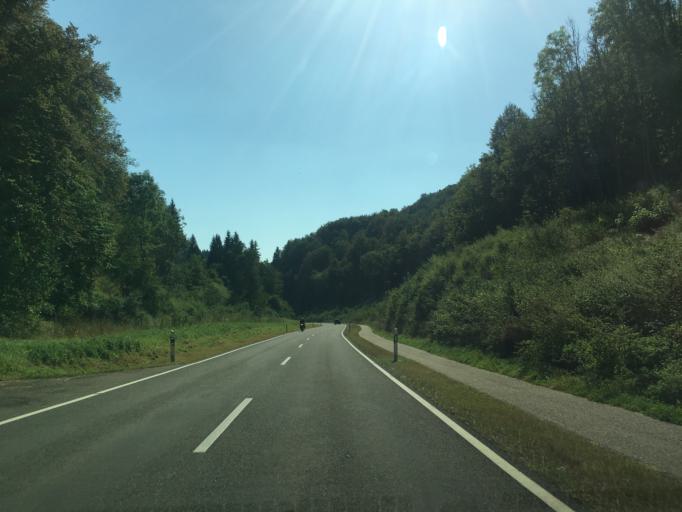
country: DE
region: Baden-Wuerttemberg
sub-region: Tuebingen Region
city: Munsingen
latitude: 48.3727
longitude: 9.4840
